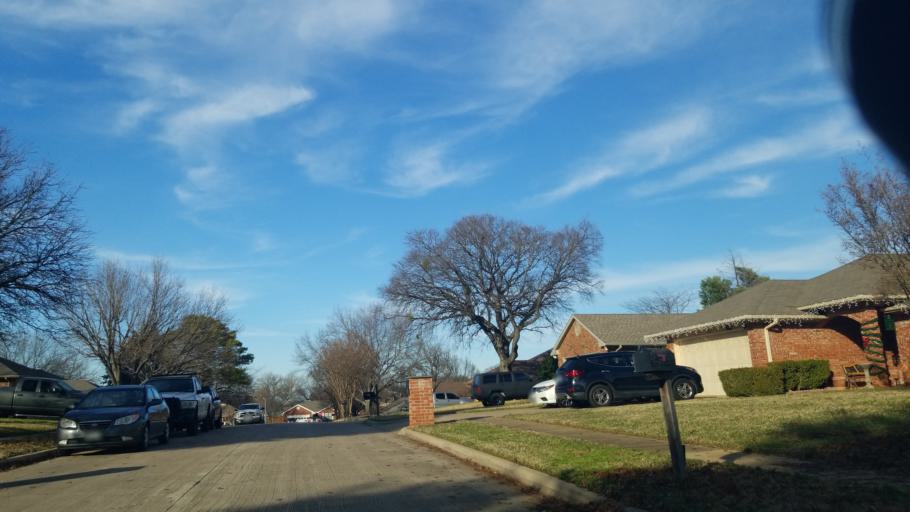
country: US
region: Texas
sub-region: Denton County
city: Corinth
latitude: 33.1380
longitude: -97.0565
